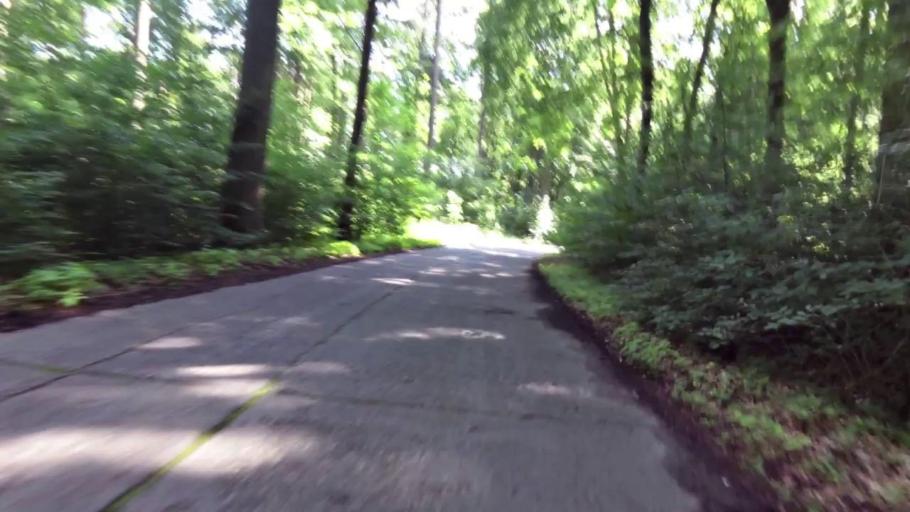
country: PL
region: West Pomeranian Voivodeship
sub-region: Powiat stargardzki
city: Dobrzany
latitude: 53.3896
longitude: 15.4616
